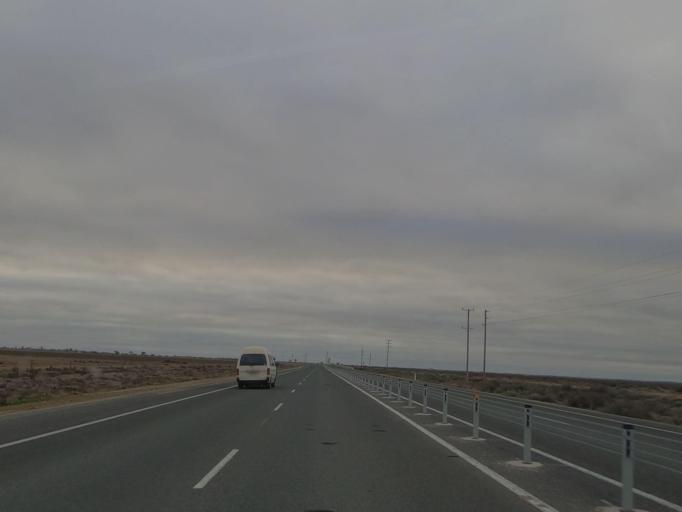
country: AU
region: Victoria
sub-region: Swan Hill
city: Swan Hill
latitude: -35.5130
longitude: 143.7259
